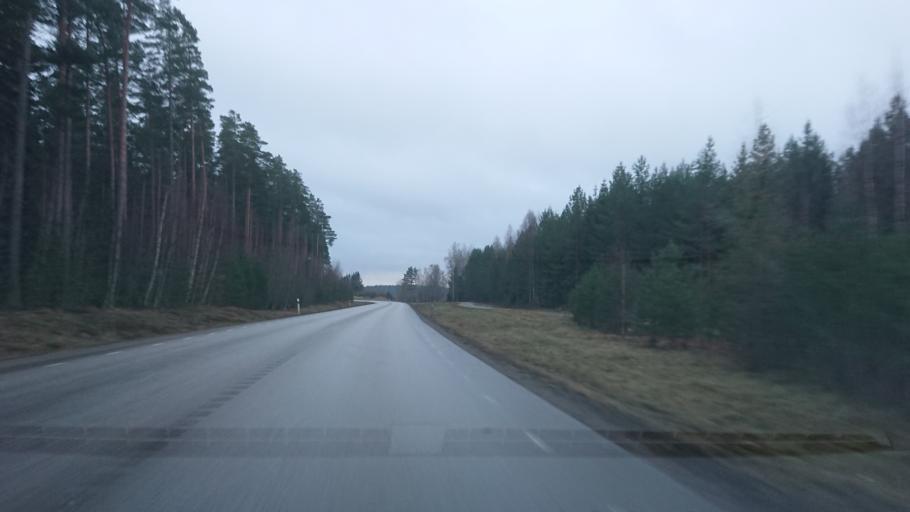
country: SE
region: Uppsala
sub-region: Osthammars Kommun
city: Bjorklinge
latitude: 60.0158
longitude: 17.5861
